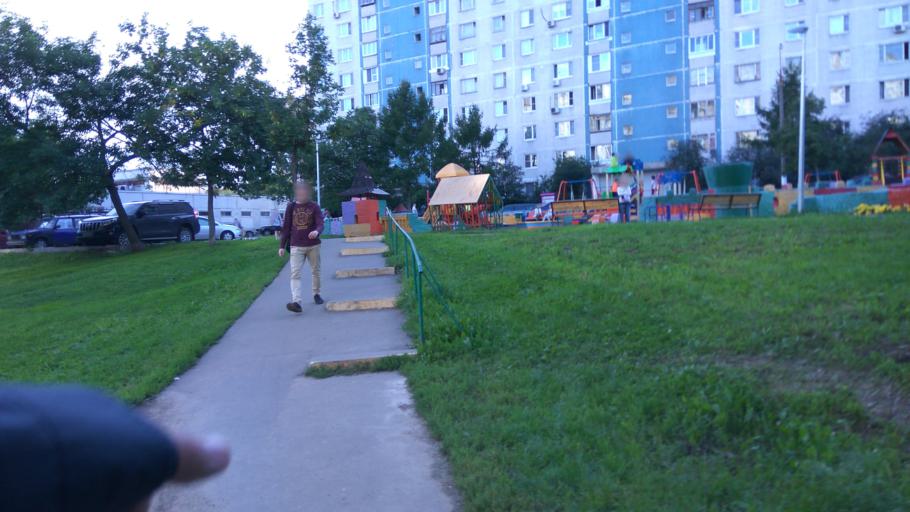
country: RU
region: Moscow
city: Tsaritsyno
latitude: 55.6255
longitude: 37.6678
